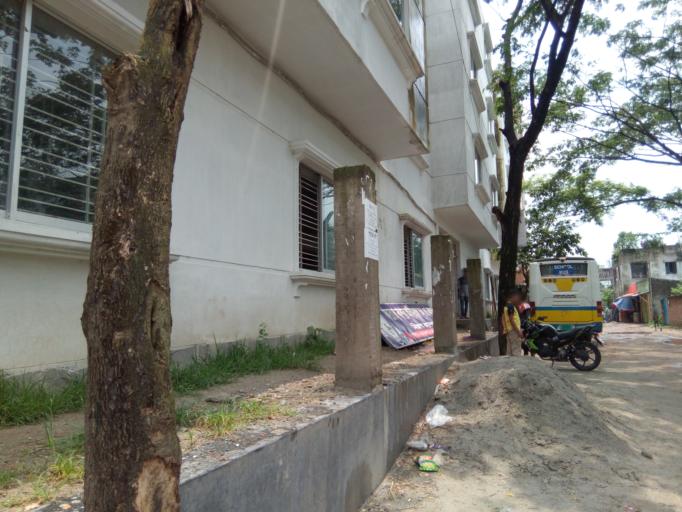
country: BD
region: Dhaka
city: Azimpur
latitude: 23.7470
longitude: 90.3487
